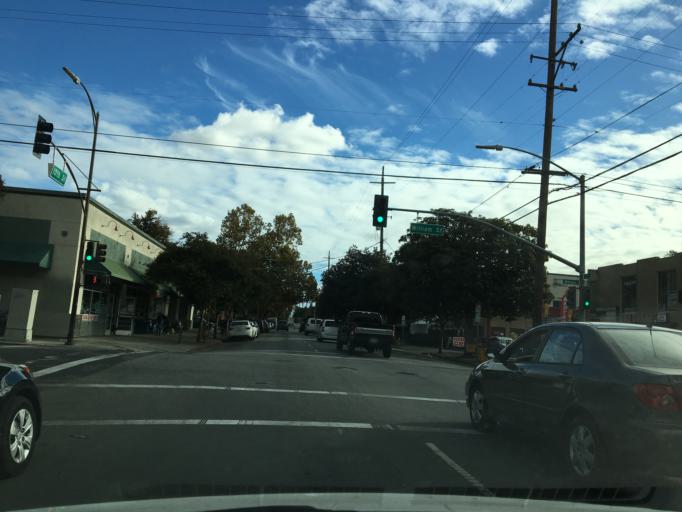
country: US
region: California
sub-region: Santa Clara County
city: San Jose
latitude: 37.3333
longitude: -121.8755
